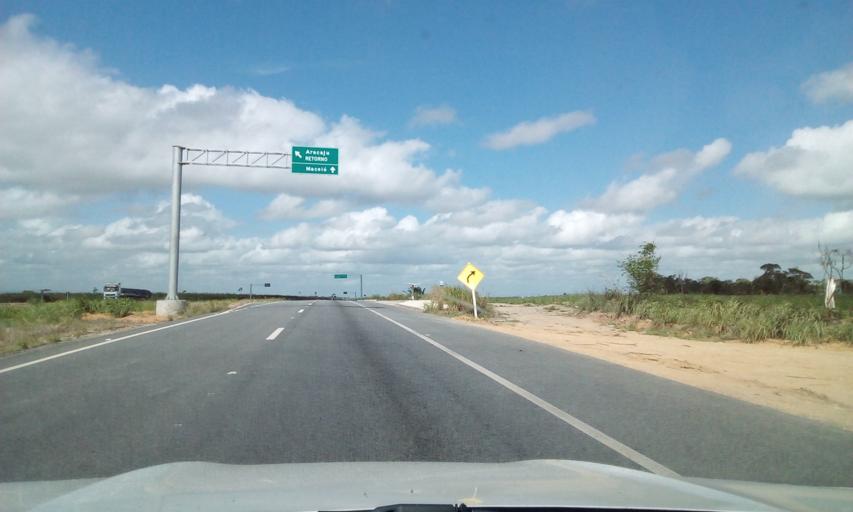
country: BR
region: Alagoas
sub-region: Rio Largo
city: Rio Largo
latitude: -9.4556
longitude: -35.8766
